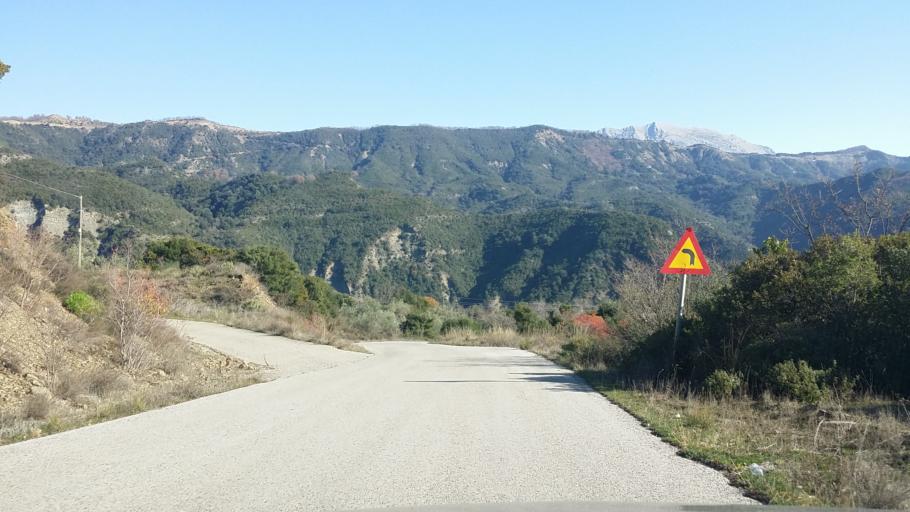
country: GR
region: West Greece
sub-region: Nomos Aitolias kai Akarnanias
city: Krikellos
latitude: 38.9998
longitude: 21.2391
